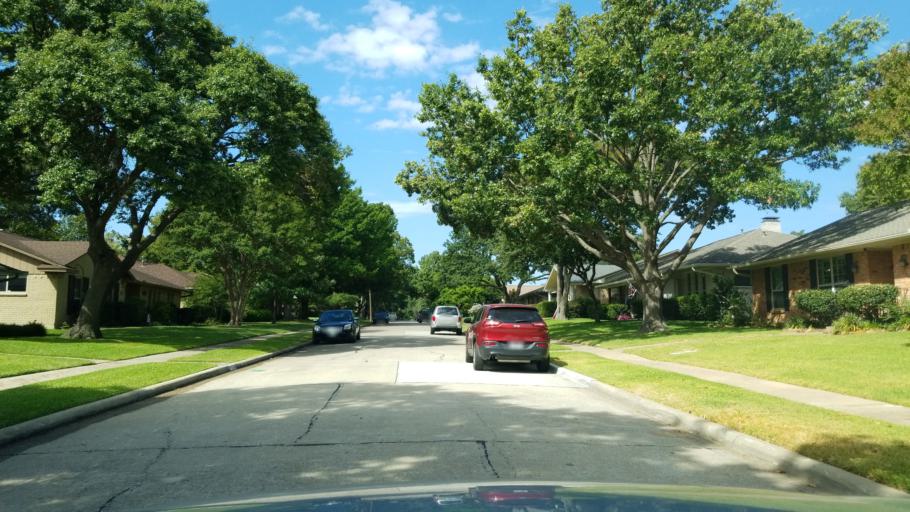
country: US
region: Texas
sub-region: Dallas County
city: Richardson
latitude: 32.9695
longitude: -96.7733
